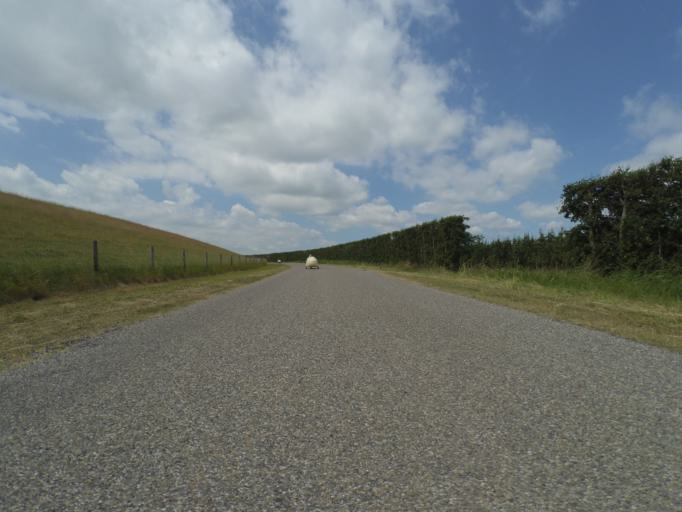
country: NL
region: Zeeland
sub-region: Gemeente Terneuzen
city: Terneuzen
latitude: 51.3985
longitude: 3.8743
